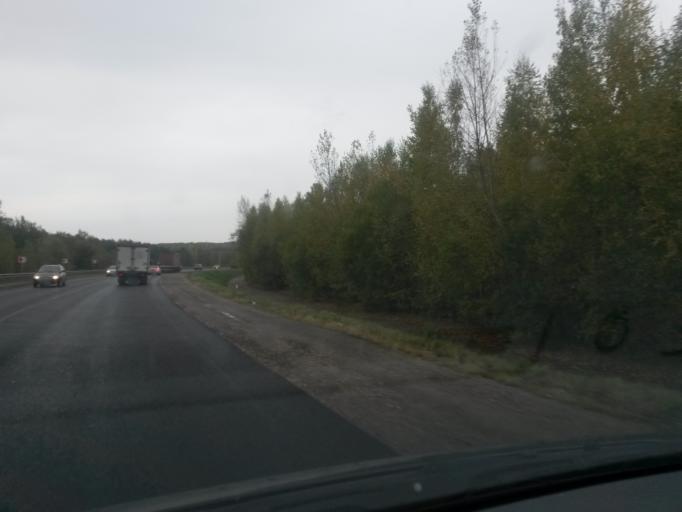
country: RU
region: Nizjnij Novgorod
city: Pamyat' Parizhskoy Kommuny
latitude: 56.0776
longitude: 44.3692
